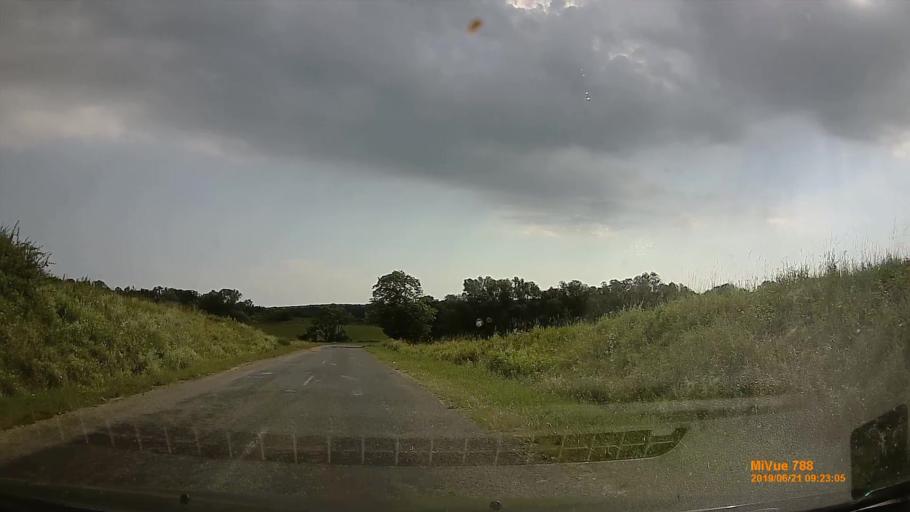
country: HU
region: Somogy
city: Taszar
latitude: 46.2490
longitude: 17.8939
